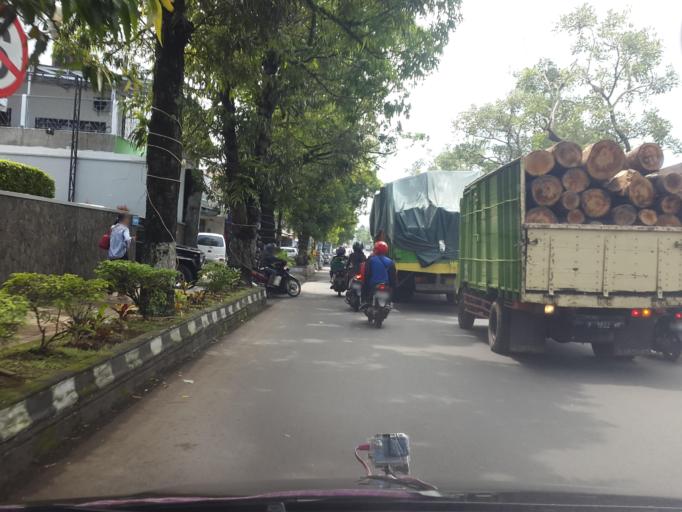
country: ID
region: Central Java
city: Purwokerto
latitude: -7.4242
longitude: 109.2260
